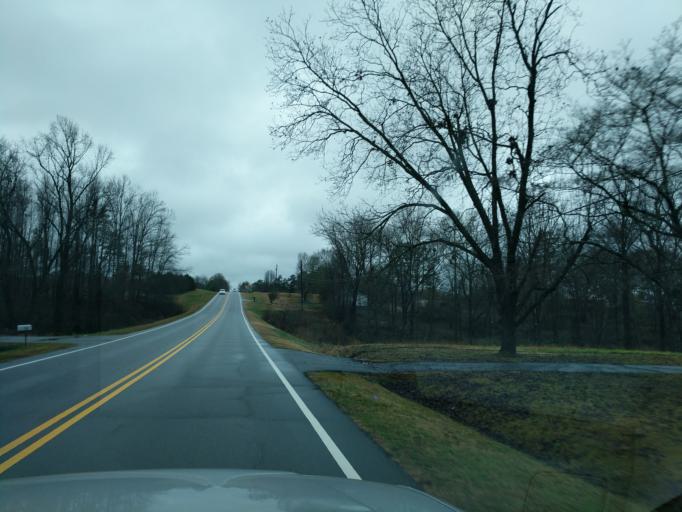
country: US
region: Georgia
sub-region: Hart County
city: Royston
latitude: 34.3585
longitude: -83.1005
